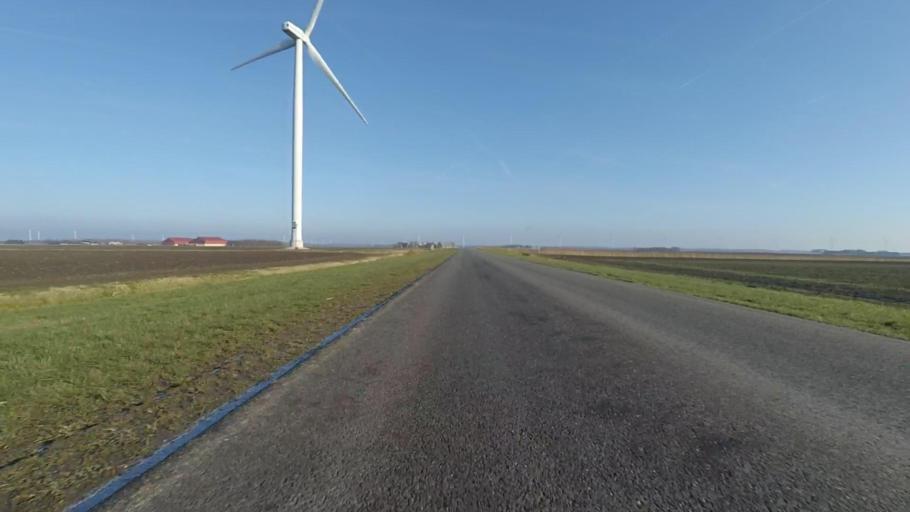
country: NL
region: Utrecht
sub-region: Gemeente Bunschoten
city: Spakenburg
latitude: 52.2995
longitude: 5.3936
